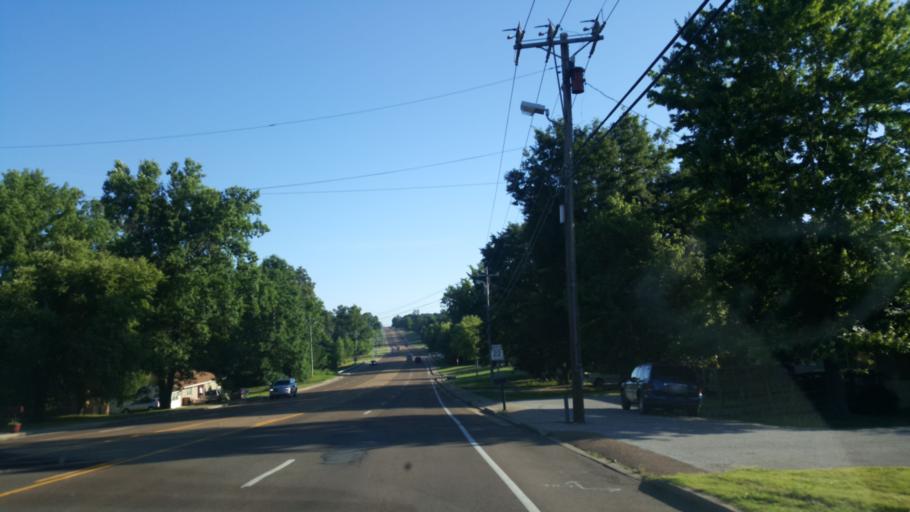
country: US
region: Tennessee
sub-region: Henderson County
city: Lexington
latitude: 35.6659
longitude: -88.3842
